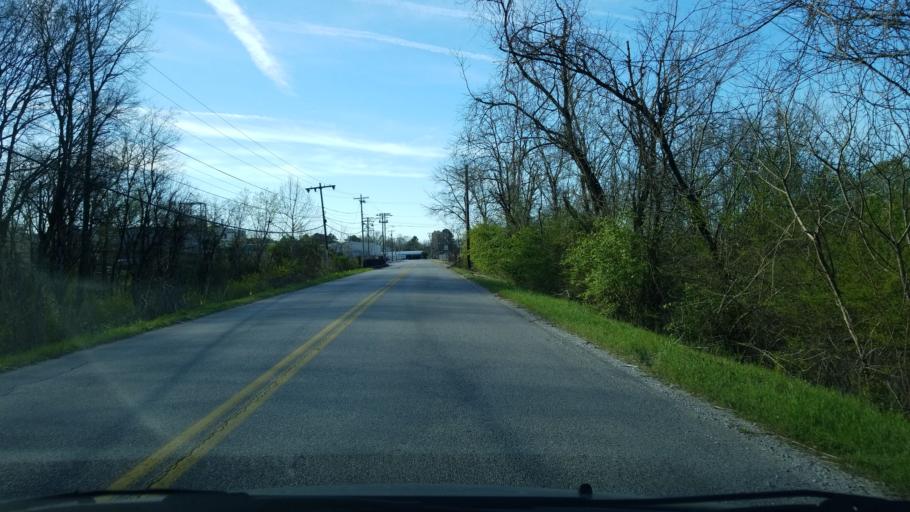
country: US
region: Tennessee
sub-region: Hamilton County
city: East Chattanooga
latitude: 35.0480
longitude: -85.1935
